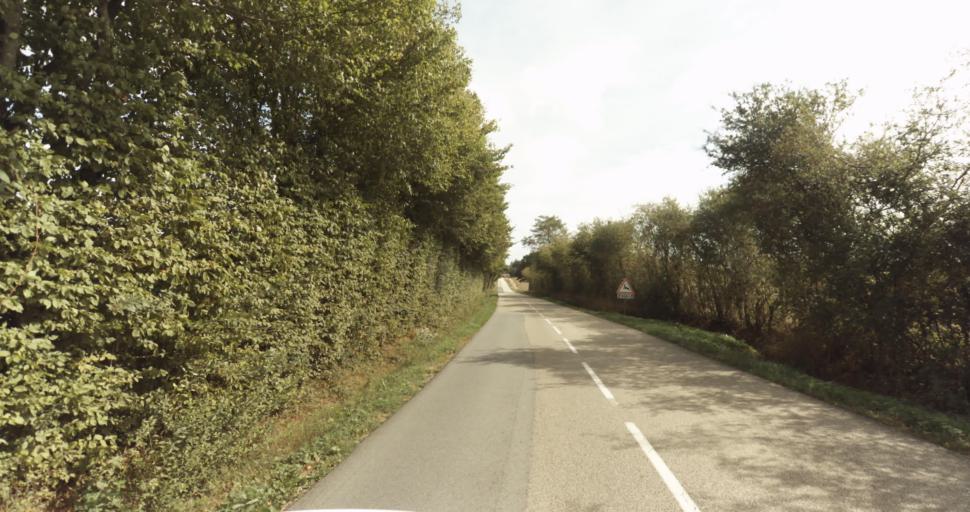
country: FR
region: Lower Normandy
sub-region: Departement de l'Orne
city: Gace
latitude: 48.7980
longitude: 0.3818
